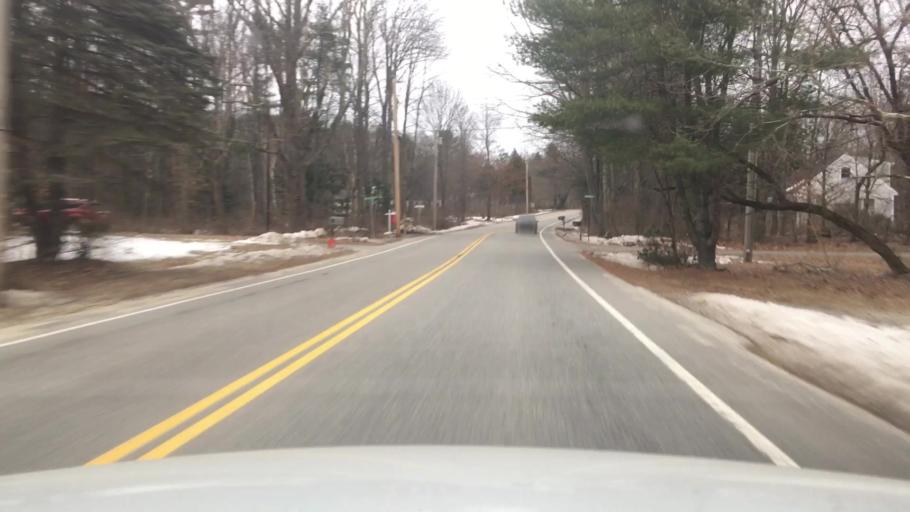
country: US
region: Maine
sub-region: Cumberland County
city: Freeport
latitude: 43.8723
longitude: -70.0651
